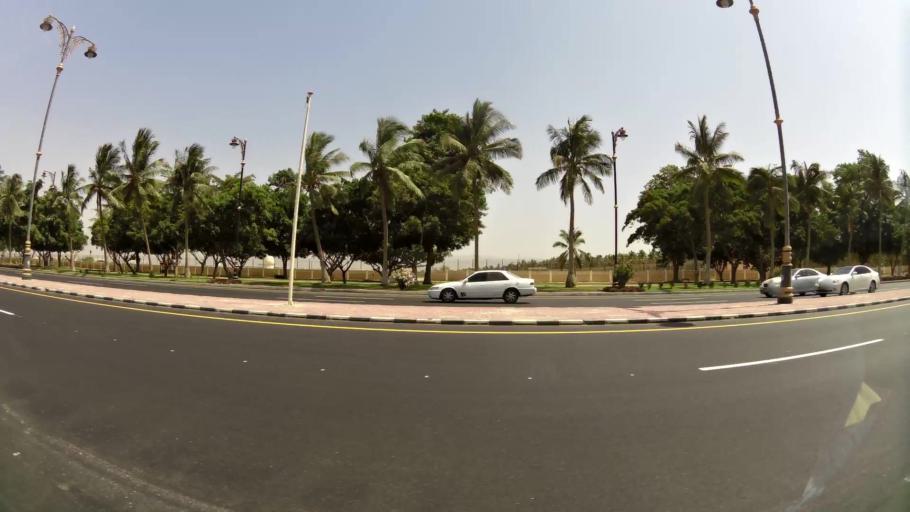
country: OM
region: Zufar
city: Salalah
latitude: 17.0244
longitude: 54.1090
